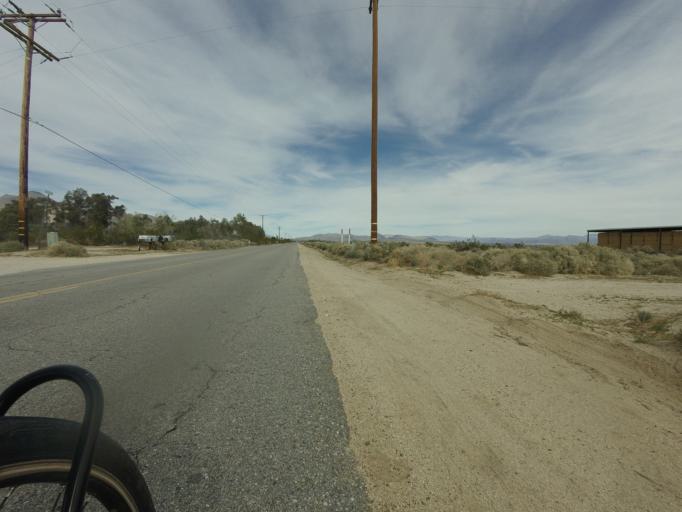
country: US
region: California
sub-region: Kern County
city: Inyokern
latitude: 35.7470
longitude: -117.8420
